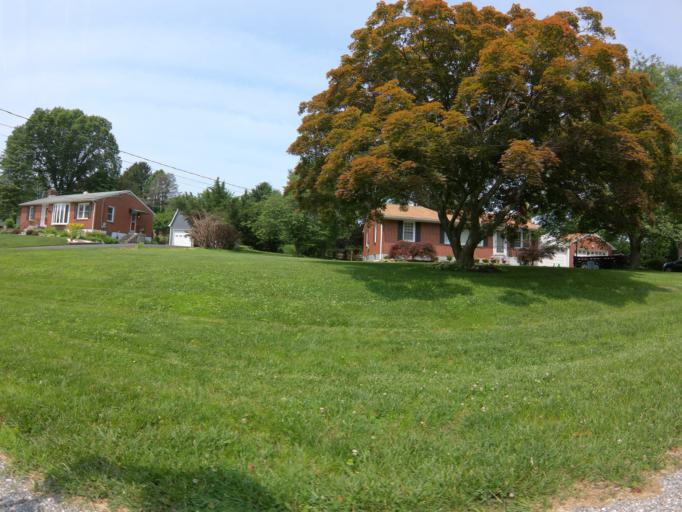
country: US
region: Maryland
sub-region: Howard County
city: Columbia
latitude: 39.2348
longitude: -76.8065
